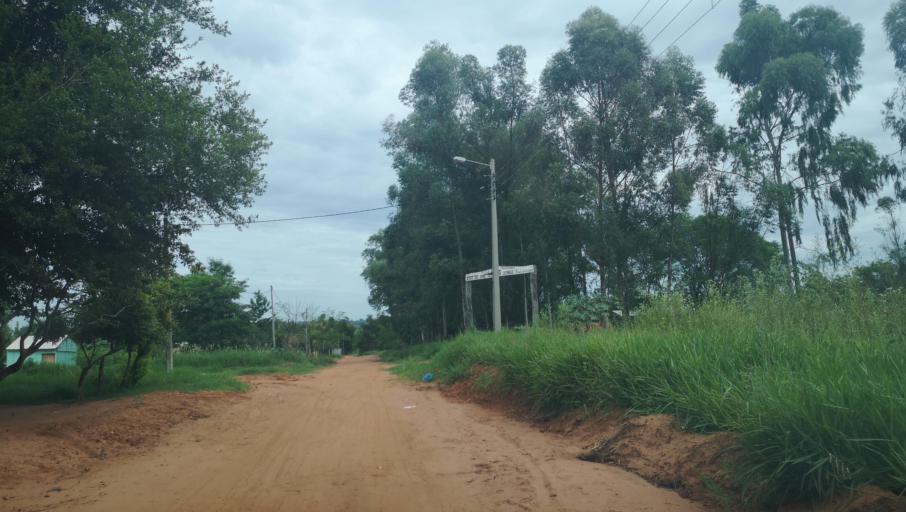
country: PY
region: San Pedro
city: Capiibary
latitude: -24.7246
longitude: -56.0219
